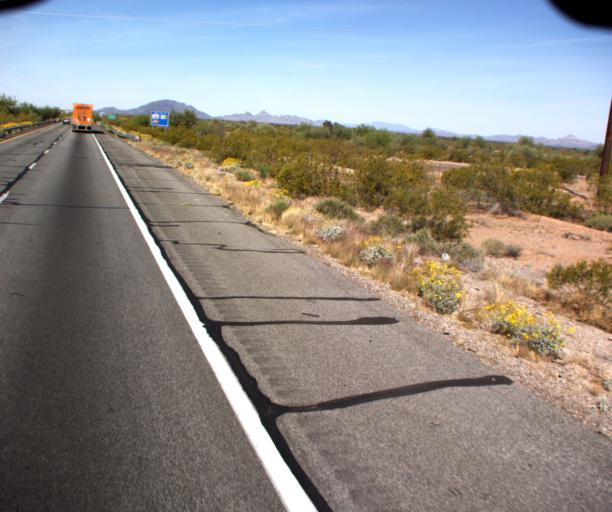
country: US
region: Arizona
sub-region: Maricopa County
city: Buckeye
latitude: 33.4928
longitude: -112.9156
